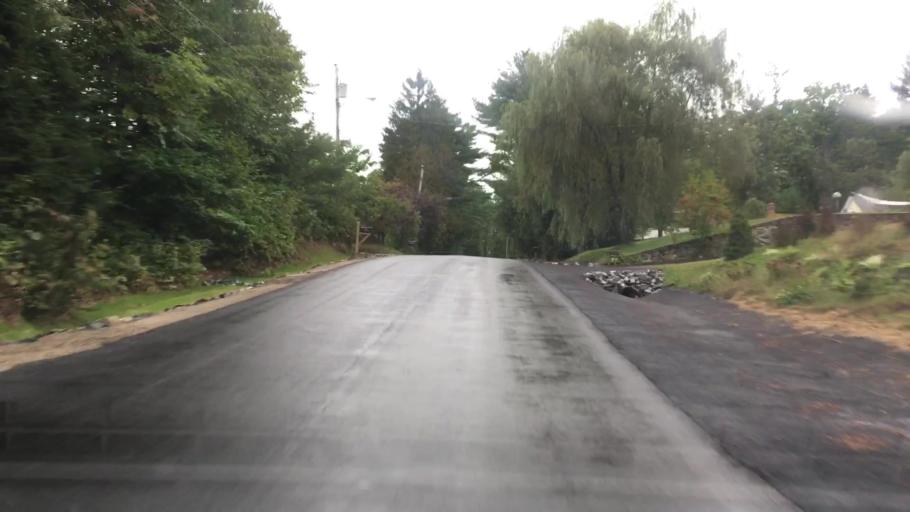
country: US
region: Maine
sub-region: Cumberland County
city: Raymond
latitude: 43.9869
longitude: -70.5607
